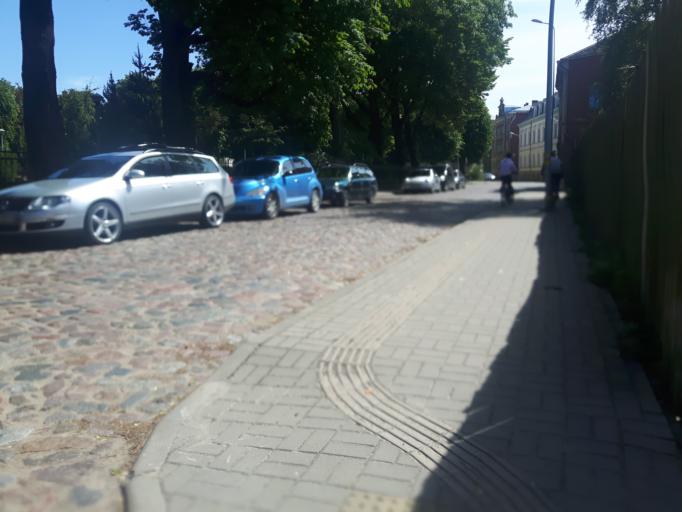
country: LV
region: Liepaja
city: Liepaja
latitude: 56.5110
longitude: 21.0012
